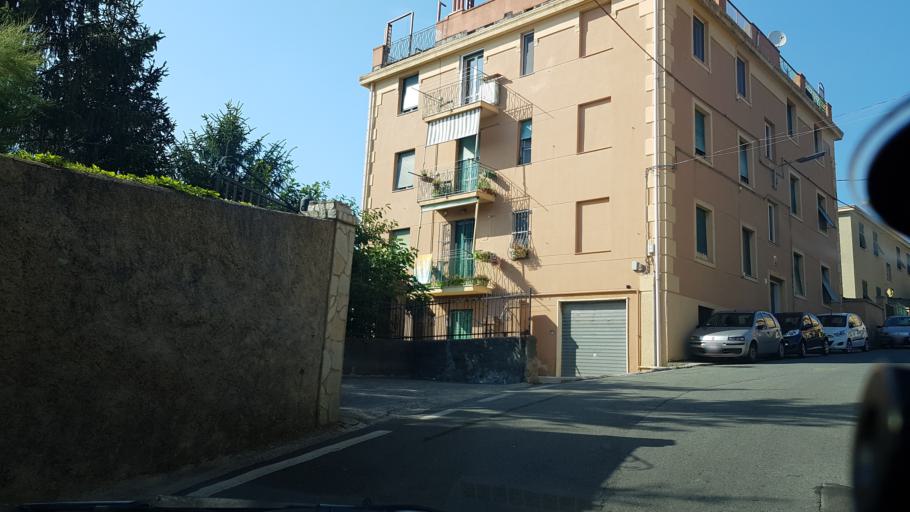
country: IT
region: Liguria
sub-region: Provincia di Genova
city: Genoa
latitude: 44.4453
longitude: 8.8996
